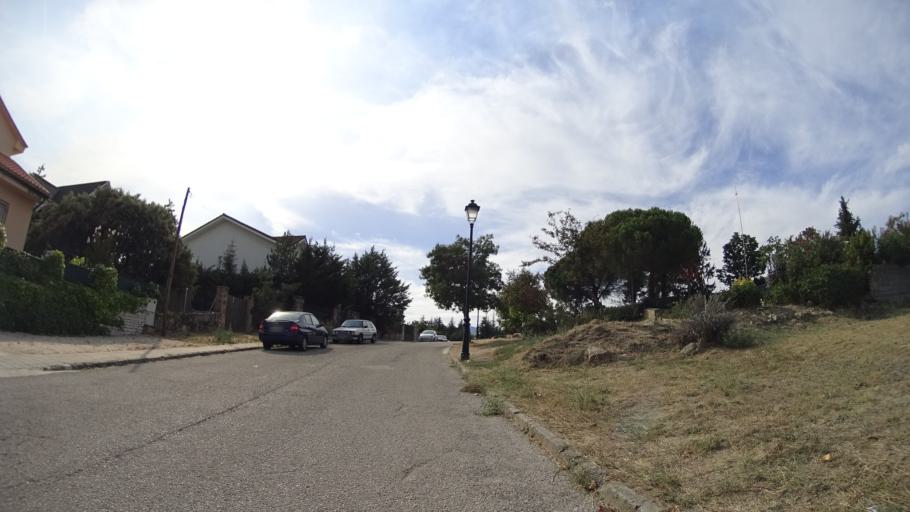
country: ES
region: Madrid
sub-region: Provincia de Madrid
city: Becerril de la Sierra
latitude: 40.7029
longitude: -3.9869
